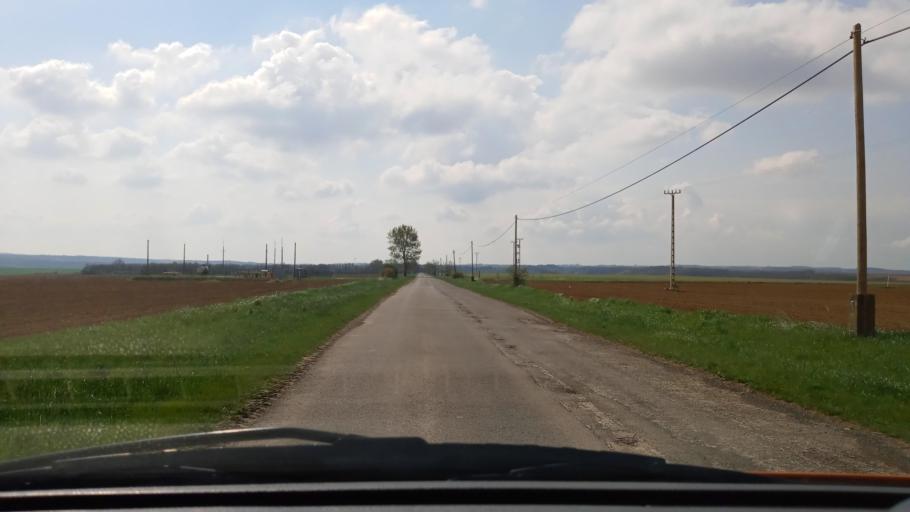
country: HU
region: Baranya
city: Pecsvarad
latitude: 46.0906
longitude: 18.5030
